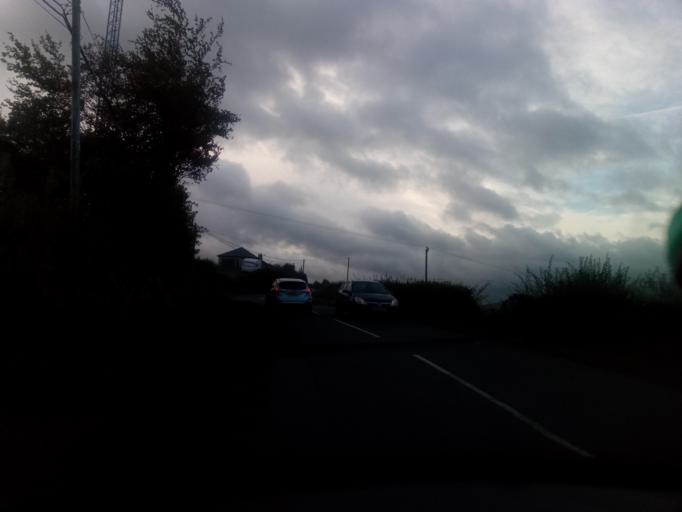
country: GB
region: Scotland
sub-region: The Scottish Borders
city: Jedburgh
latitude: 55.3957
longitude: -2.6498
